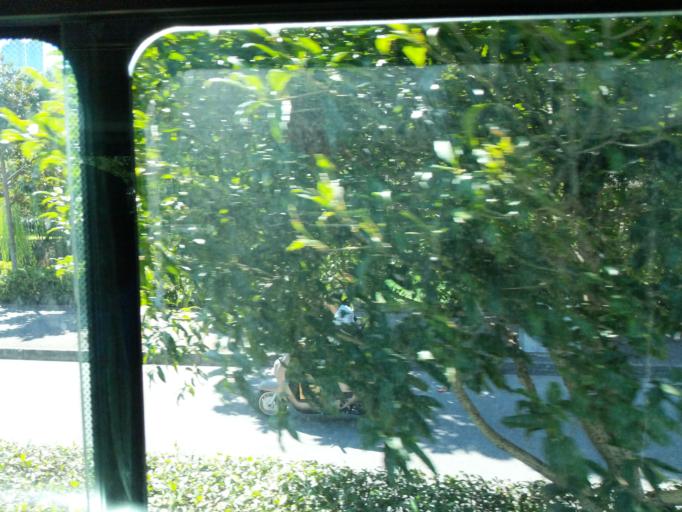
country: CN
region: Jiangsu Sheng
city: Pingjianglu
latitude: 31.3222
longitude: 120.6585
